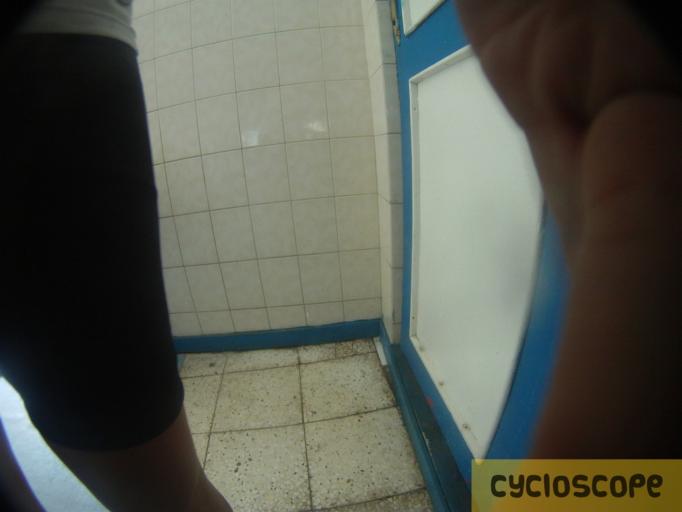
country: GE
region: Ajaria
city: Kobuleti
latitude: 41.8417
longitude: 41.7785
